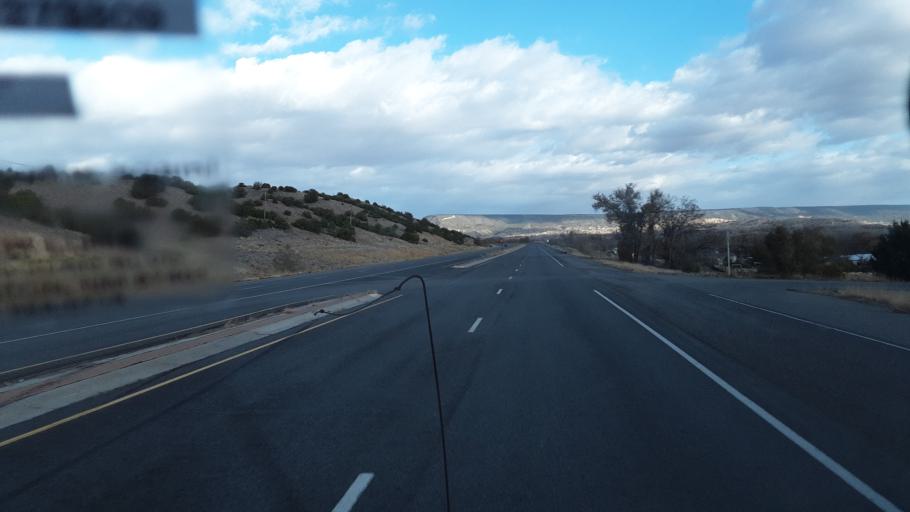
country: US
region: New Mexico
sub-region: Rio Arriba County
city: Ohkay Owingeh
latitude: 36.0294
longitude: -106.0934
